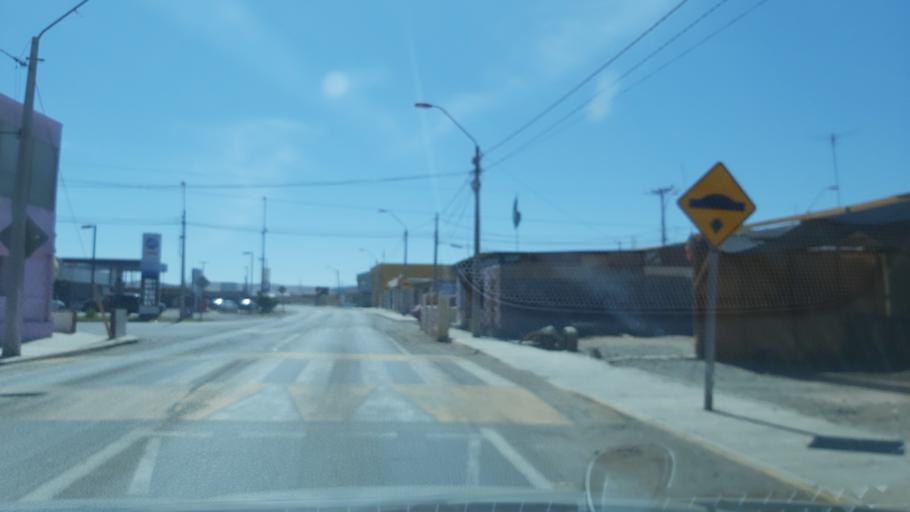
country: CL
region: Atacama
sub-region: Provincia de Chanaral
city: Diego de Almagro
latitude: -26.3907
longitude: -70.0388
